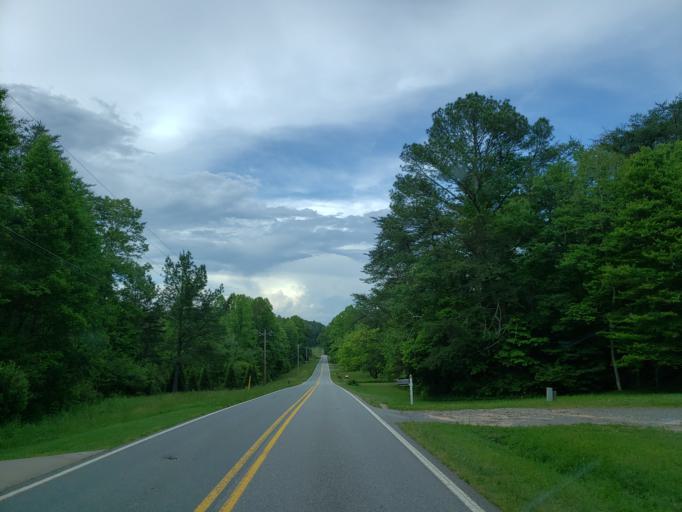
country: US
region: Georgia
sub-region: Fannin County
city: Blue Ridge
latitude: 34.8578
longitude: -84.3749
